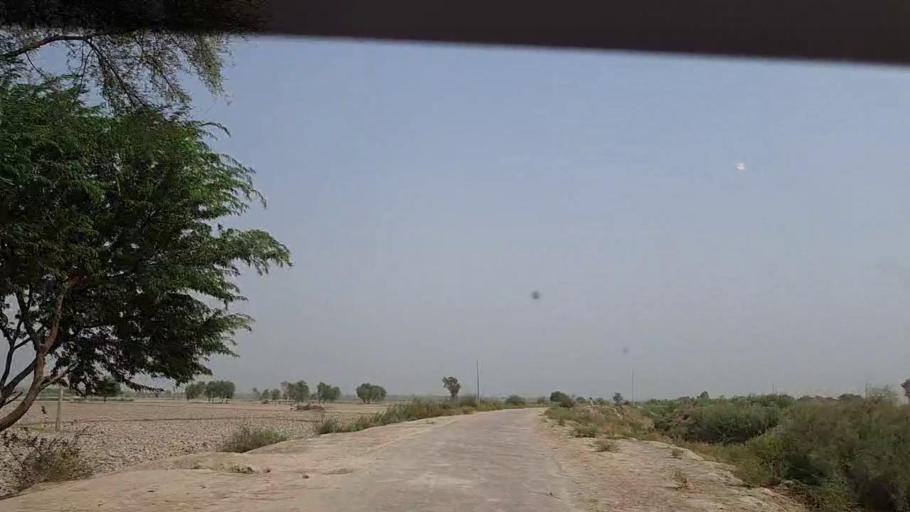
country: PK
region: Sindh
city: Khairpur Nathan Shah
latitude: 27.0456
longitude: 67.6855
